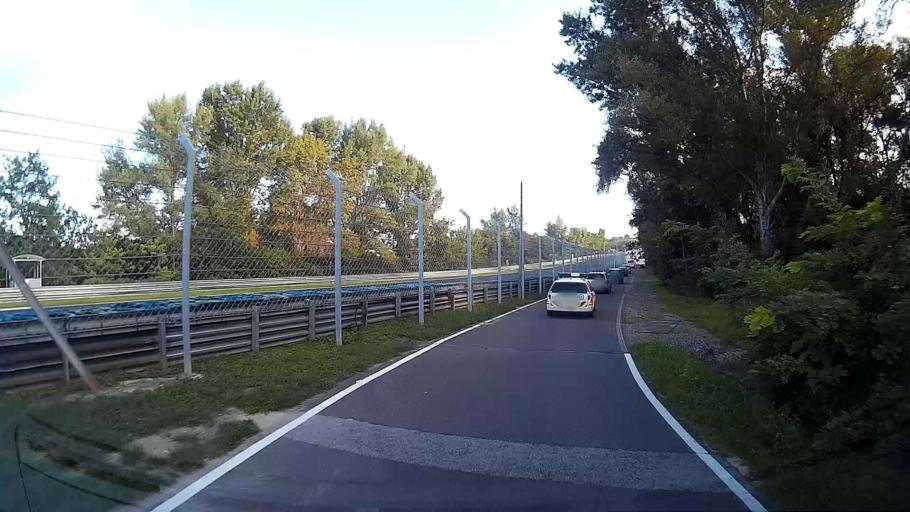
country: HU
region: Pest
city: Mogyorod
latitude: 47.5837
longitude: 19.2488
